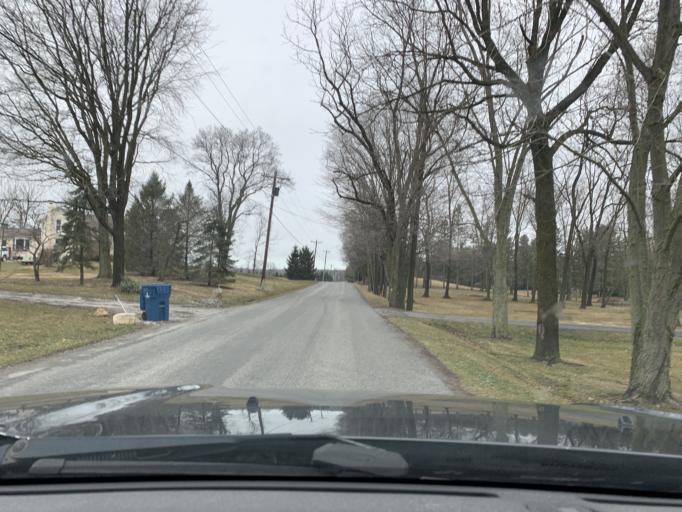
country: US
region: Indiana
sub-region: Porter County
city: Chesterton
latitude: 41.5994
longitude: -86.9899
